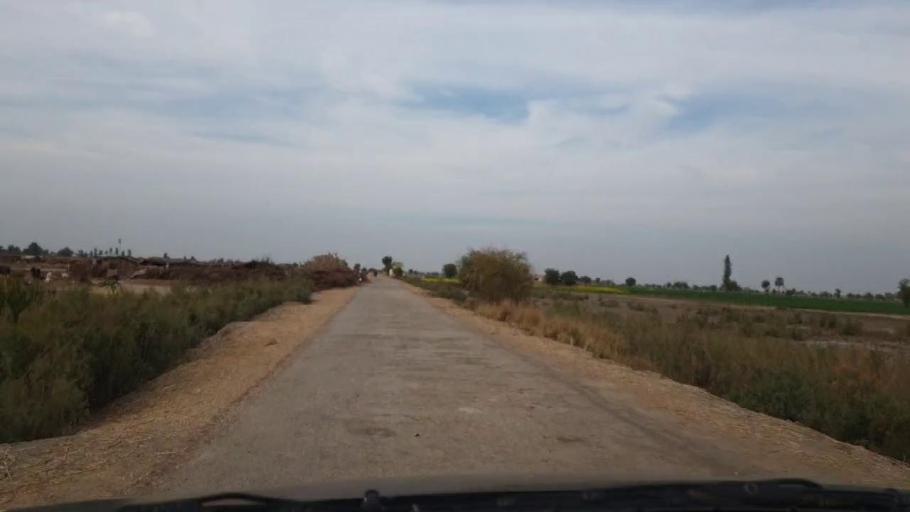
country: PK
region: Sindh
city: Khadro
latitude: 26.1589
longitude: 68.7304
